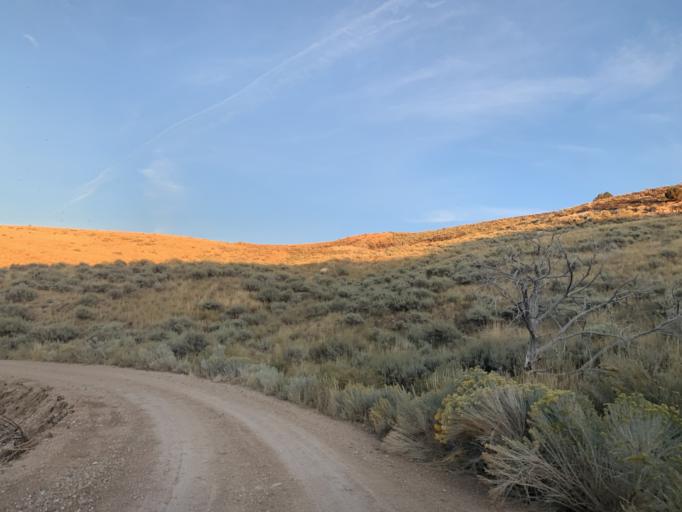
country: US
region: Utah
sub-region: Utah County
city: West Mountain
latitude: 40.0983
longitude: -111.8266
